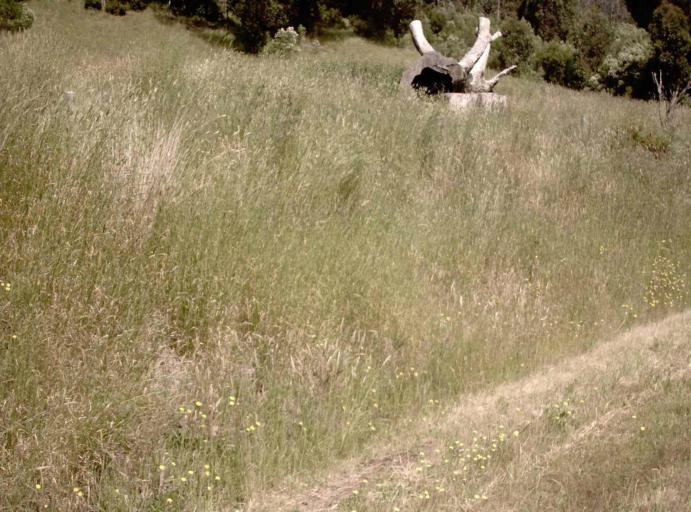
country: AU
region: Victoria
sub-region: Latrobe
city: Traralgon
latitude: -38.3405
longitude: 146.5730
